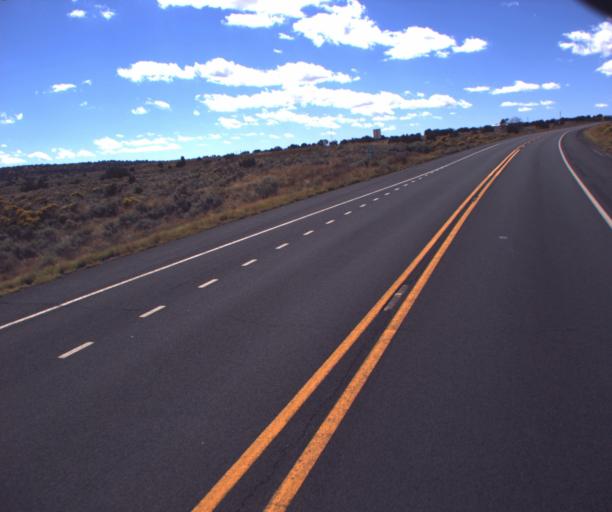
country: US
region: Arizona
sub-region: Apache County
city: Houck
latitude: 35.1958
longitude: -109.3329
